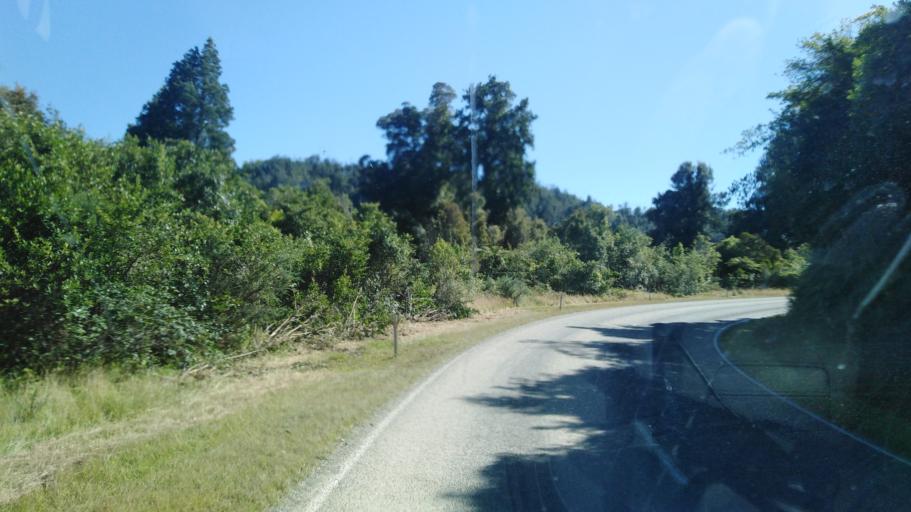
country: NZ
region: West Coast
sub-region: Buller District
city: Westport
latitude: -41.5301
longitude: 171.9938
